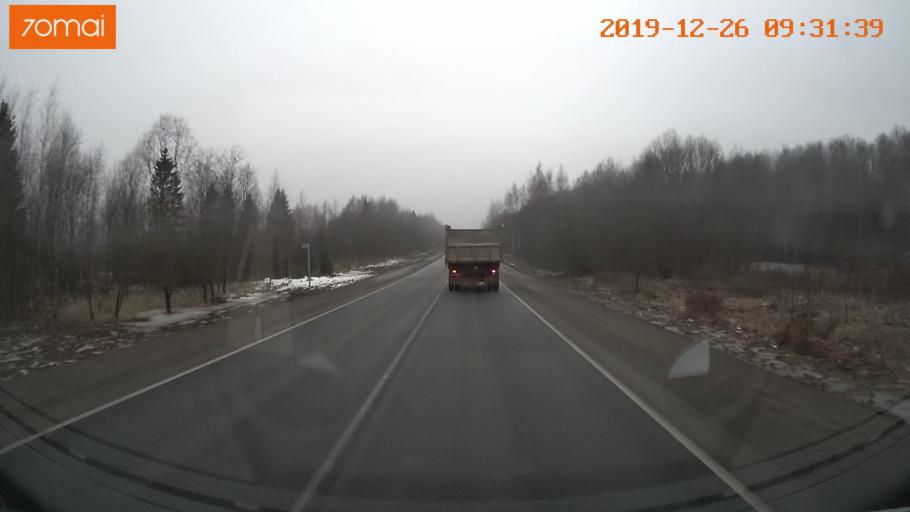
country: RU
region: Vologda
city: Gryazovets
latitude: 59.0709
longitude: 40.1257
